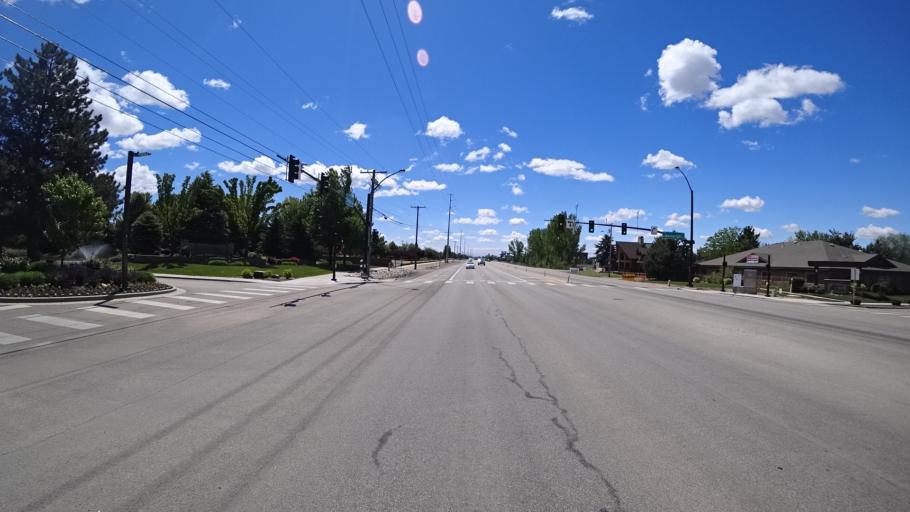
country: US
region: Idaho
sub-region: Ada County
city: Meridian
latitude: 43.6415
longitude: -116.3543
